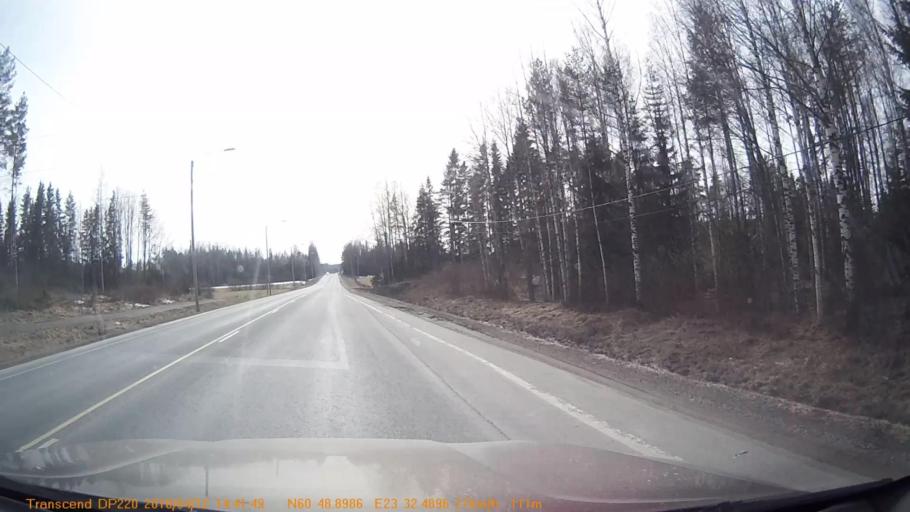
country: FI
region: Haeme
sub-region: Forssa
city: Jokioinen
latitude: 60.8148
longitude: 23.5412
